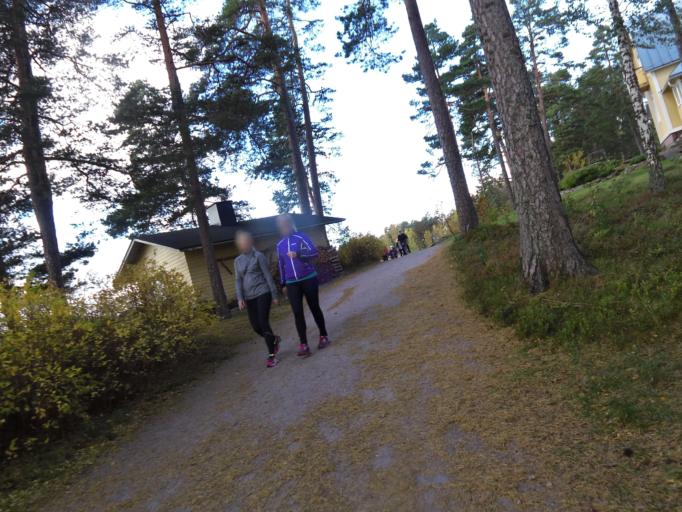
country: FI
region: Uusimaa
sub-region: Helsinki
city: Koukkuniemi
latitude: 60.1503
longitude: 24.7618
